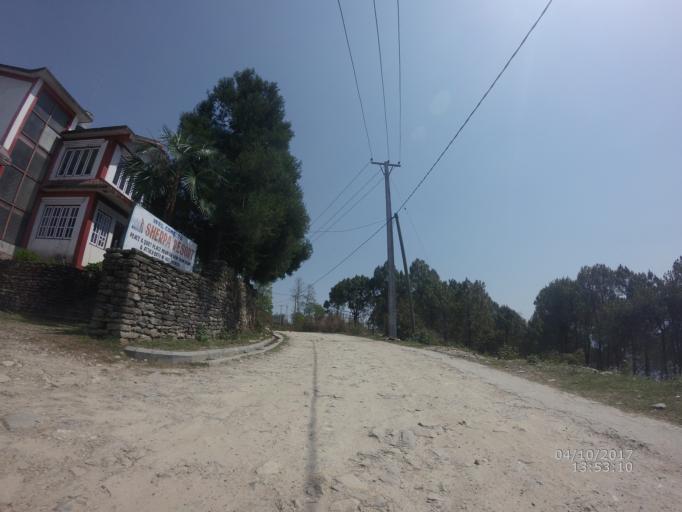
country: NP
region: Western Region
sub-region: Gandaki Zone
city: Pokhara
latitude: 28.2488
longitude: 83.9446
